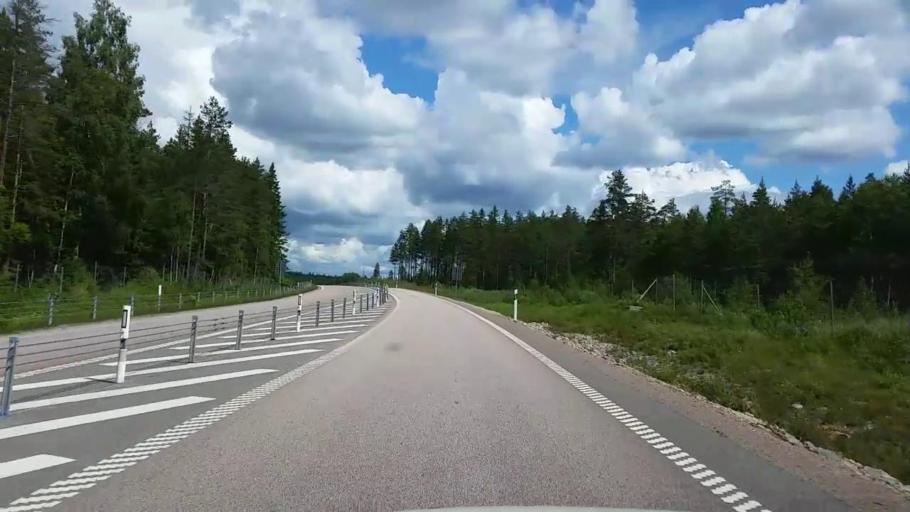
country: SE
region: Vaestmanland
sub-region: Norbergs Kommun
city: Norberg
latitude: 60.0849
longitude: 15.9859
